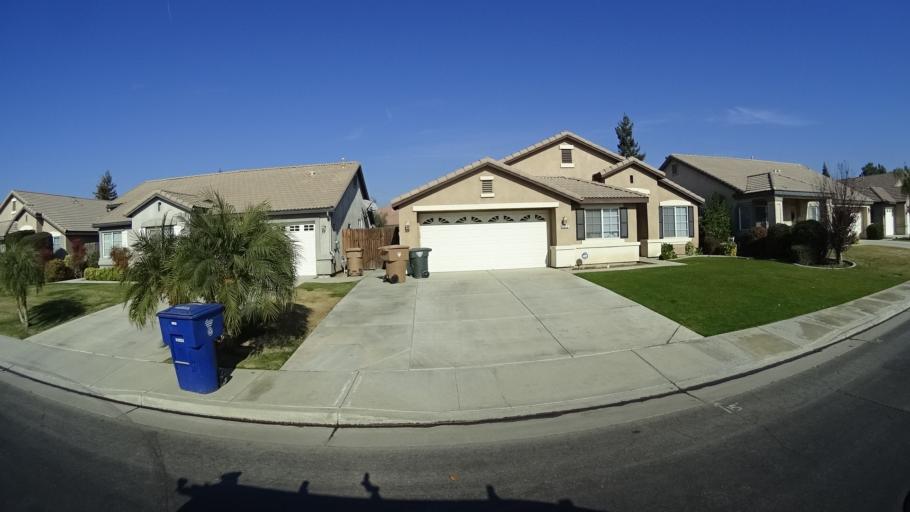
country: US
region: California
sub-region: Kern County
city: Greenacres
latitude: 35.3139
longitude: -119.1128
